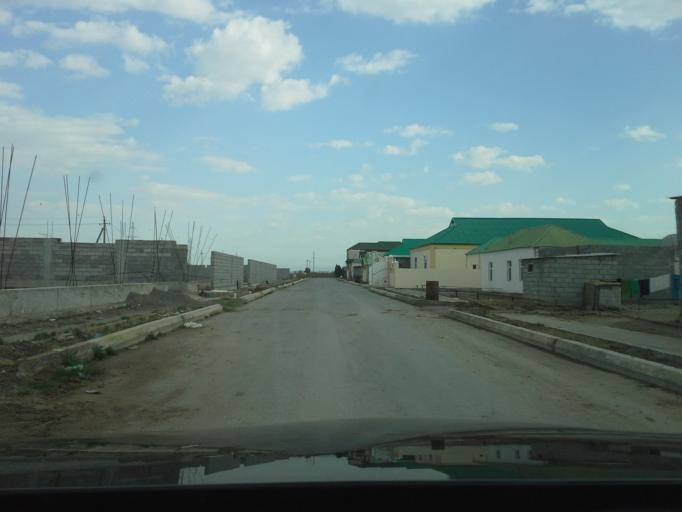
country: TM
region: Ahal
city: Ashgabat
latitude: 37.9945
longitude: 58.2980
